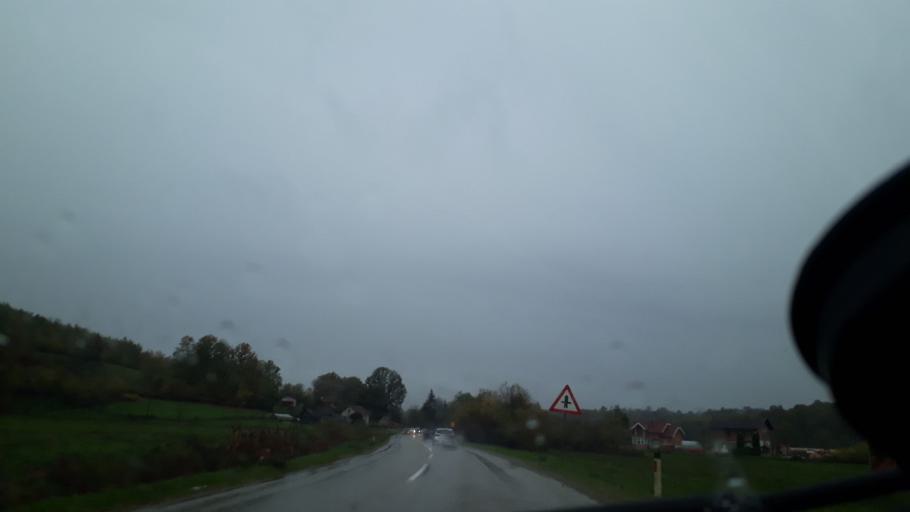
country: BA
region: Republika Srpska
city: Maglajani
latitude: 44.8618
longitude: 17.4364
